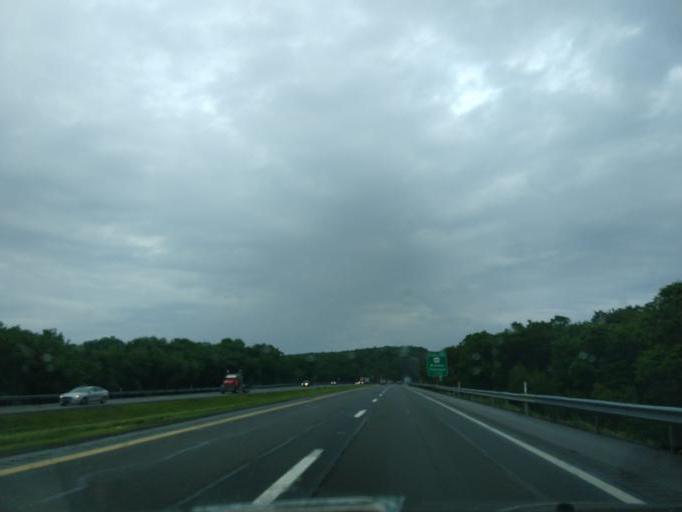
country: US
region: Pennsylvania
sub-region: Schuylkill County
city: McAdoo
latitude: 40.8918
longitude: -76.0247
